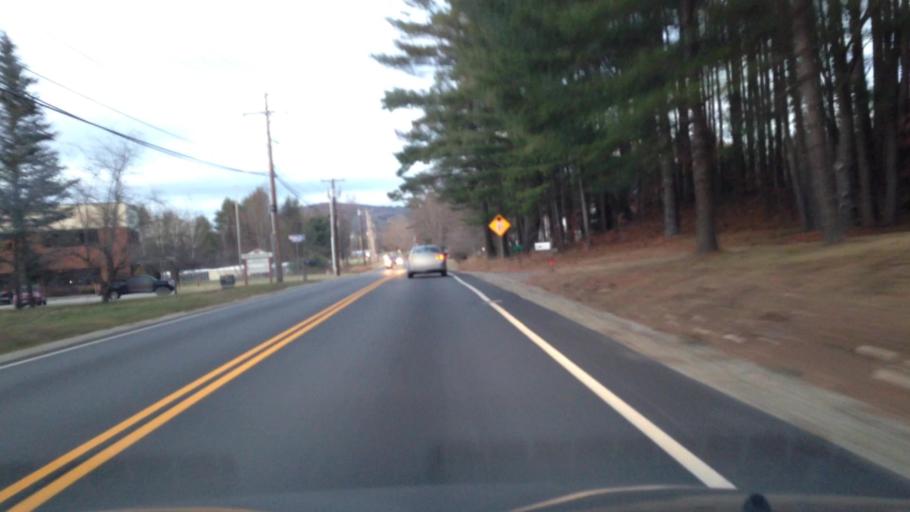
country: US
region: New Hampshire
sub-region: Cheshire County
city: Swanzey
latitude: 42.8922
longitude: -72.2651
